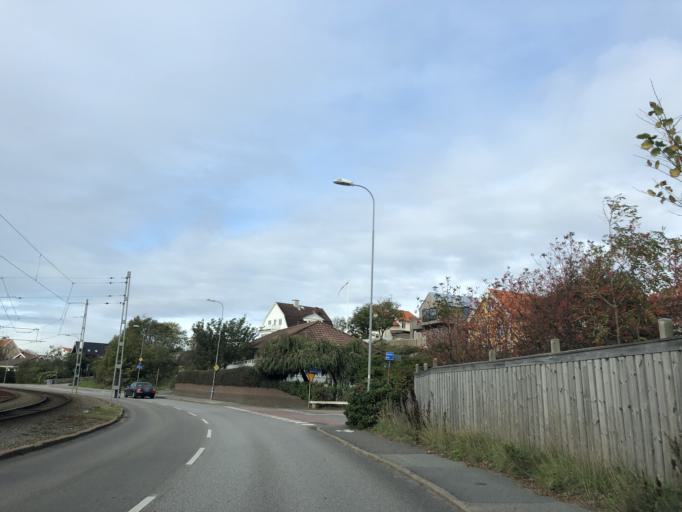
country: SE
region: Vaestra Goetaland
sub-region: Goteborg
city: Majorna
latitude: 57.6694
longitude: 11.8567
